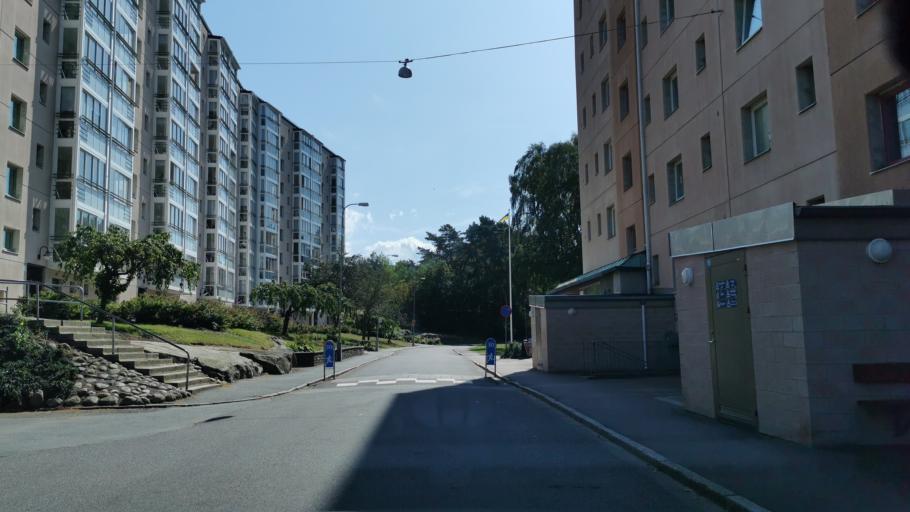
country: SE
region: Vaestra Goetaland
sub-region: Goteborg
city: Majorna
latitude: 57.6624
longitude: 11.9187
